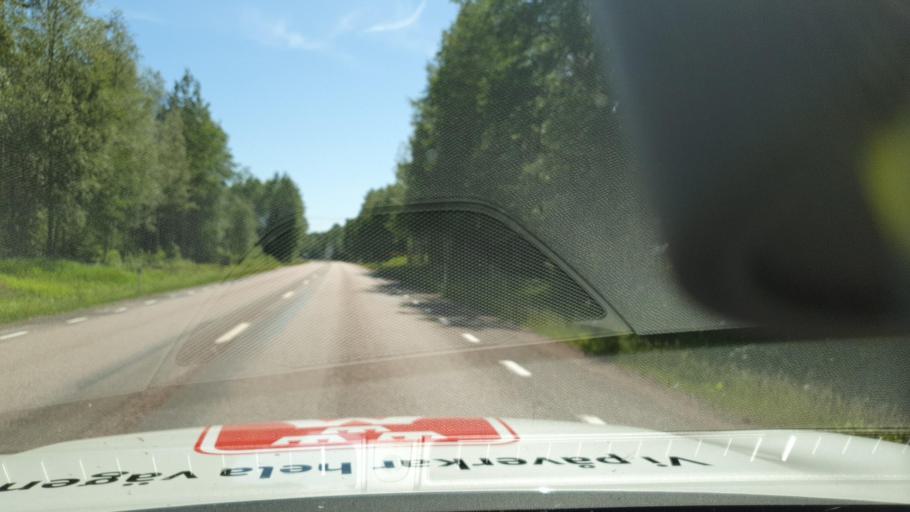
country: SE
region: Vaermland
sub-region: Kristinehamns Kommun
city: Kristinehamn
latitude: 59.3434
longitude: 14.1307
